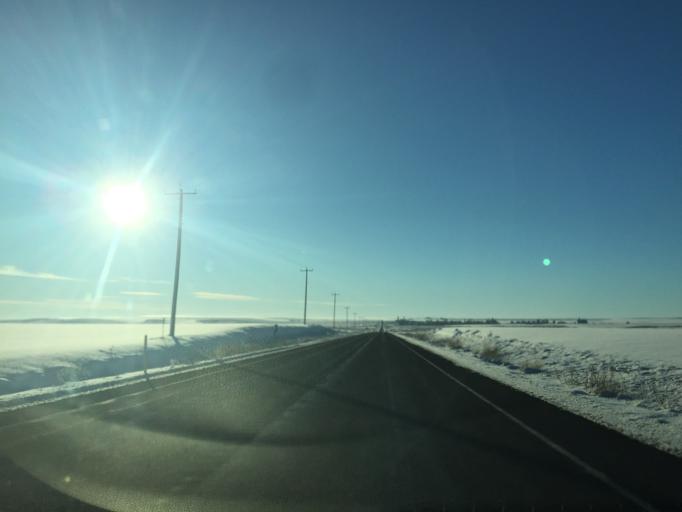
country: US
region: Washington
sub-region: Okanogan County
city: Coulee Dam
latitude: 47.7205
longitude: -118.8974
